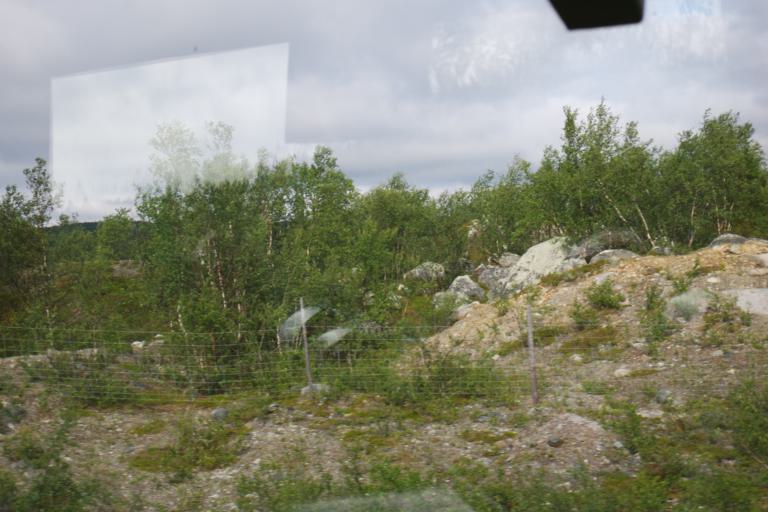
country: NO
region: Finnmark Fylke
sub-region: Karasjok
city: Karasjohka
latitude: 69.7441
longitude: 25.2266
